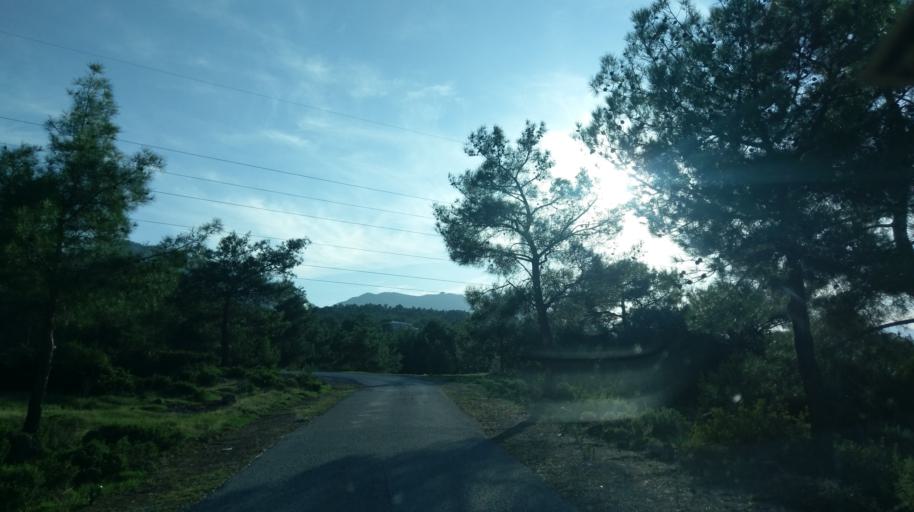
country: CY
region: Ammochostos
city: Lefkonoiko
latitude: 35.3303
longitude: 33.5856
